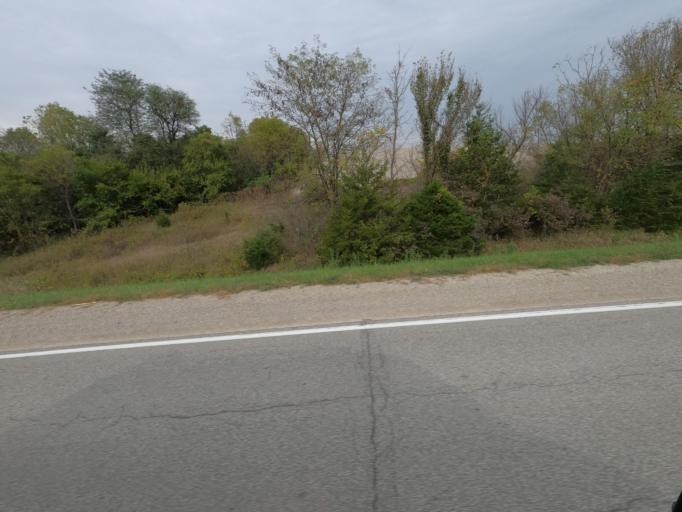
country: US
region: Iowa
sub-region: Van Buren County
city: Keosauqua
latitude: 40.8659
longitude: -92.1427
